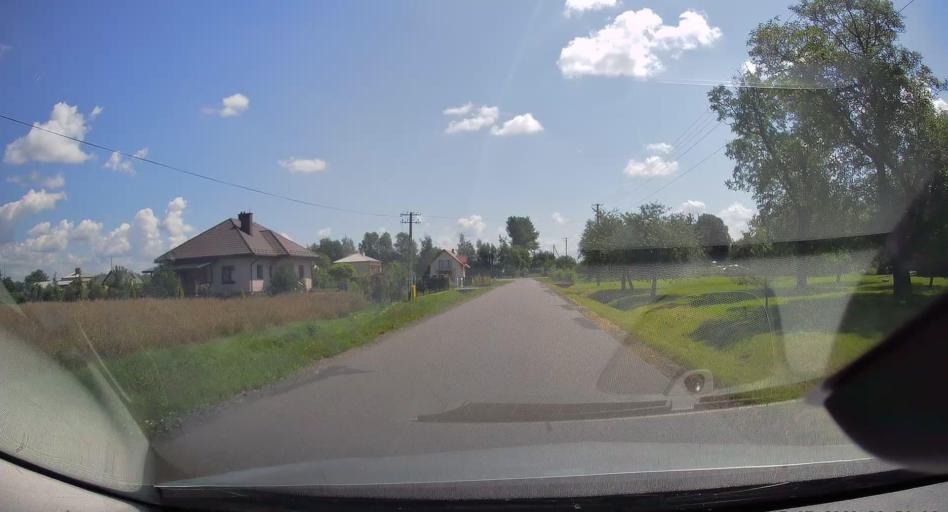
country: PL
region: Subcarpathian Voivodeship
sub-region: Powiat jaroslawski
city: Sosnica
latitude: 49.8748
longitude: 22.8568
